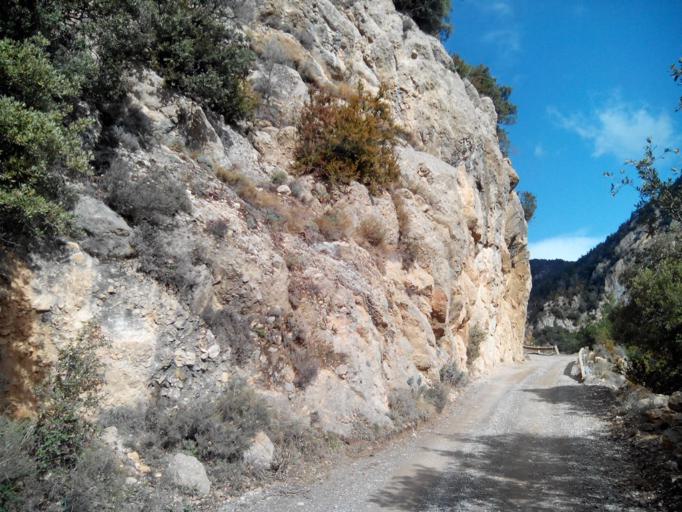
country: ES
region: Catalonia
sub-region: Provincia de Barcelona
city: Vilada
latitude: 42.1706
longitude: 1.9303
